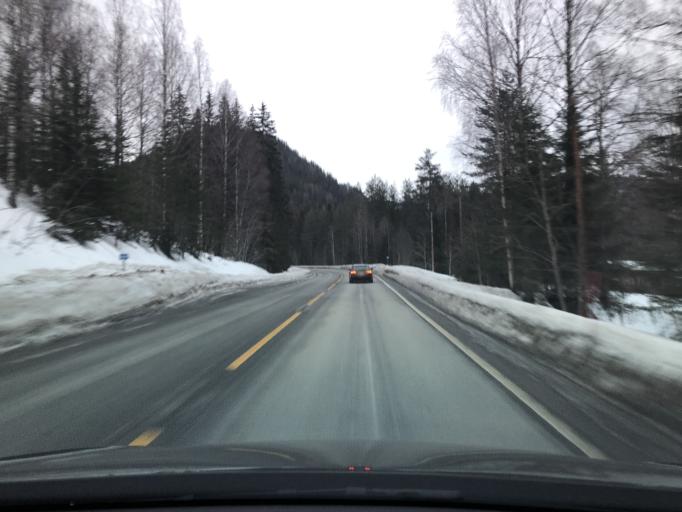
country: NO
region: Oppland
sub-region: Etnedal
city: Bruflat
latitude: 60.6673
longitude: 9.7428
